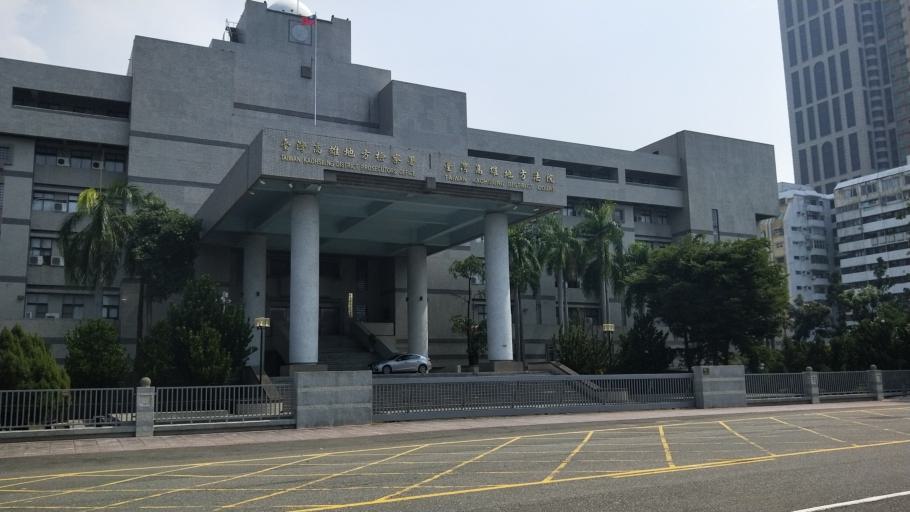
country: TW
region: Kaohsiung
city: Kaohsiung
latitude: 22.6262
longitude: 120.2893
